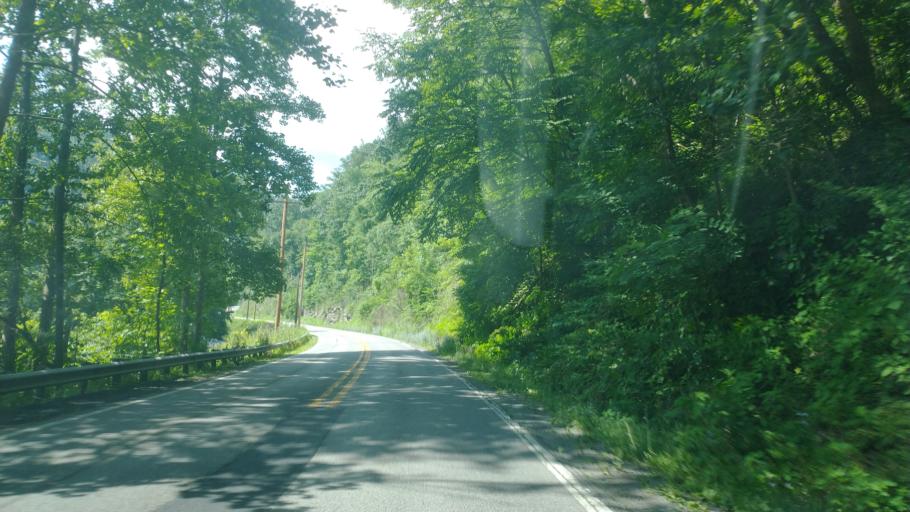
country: US
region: West Virginia
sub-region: McDowell County
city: Welch
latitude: 37.4261
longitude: -81.5115
